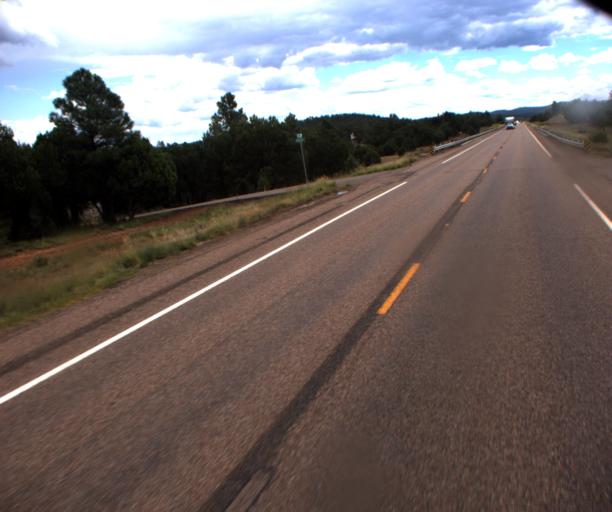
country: US
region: Arizona
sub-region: Navajo County
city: Linden
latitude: 34.3255
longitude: -110.2578
